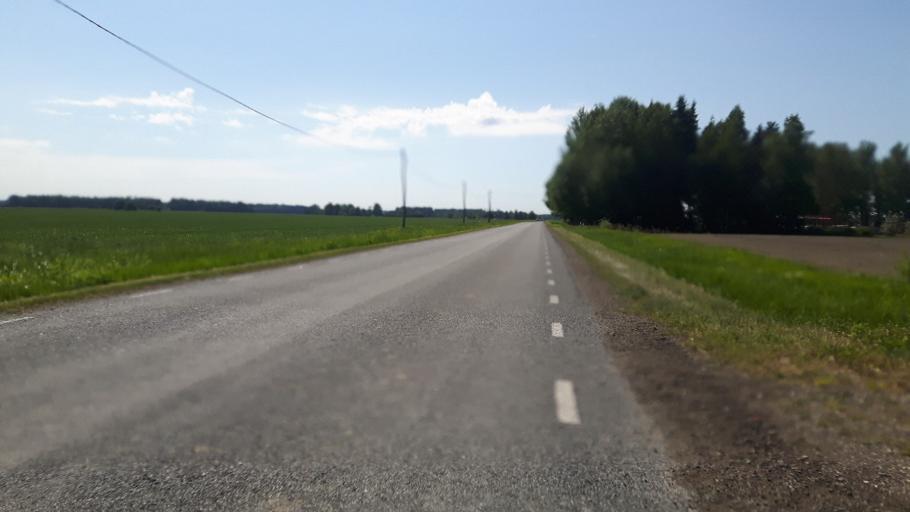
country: EE
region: Paernumaa
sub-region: Vaendra vald (alev)
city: Vandra
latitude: 58.6219
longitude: 25.0210
